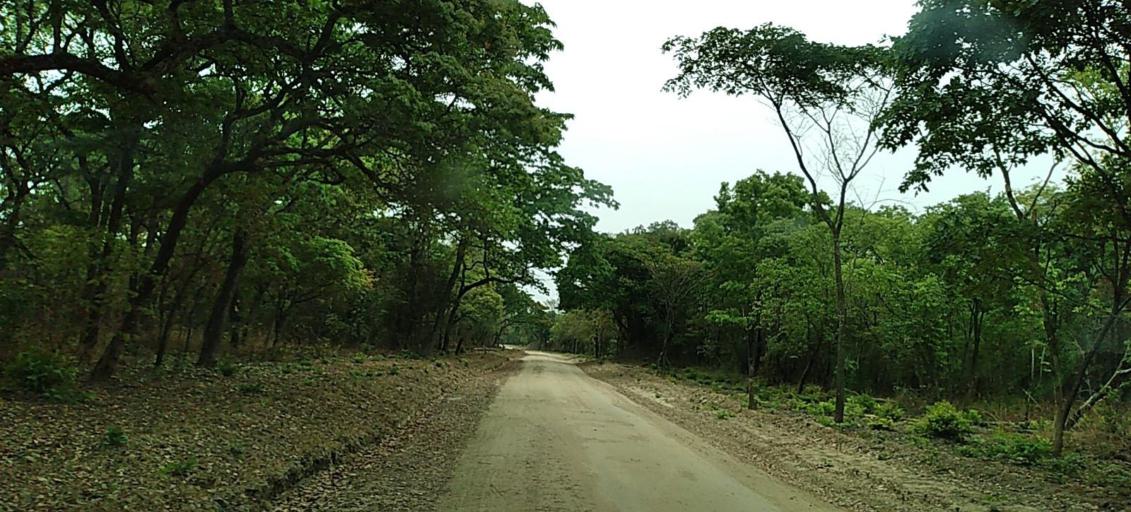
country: ZM
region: North-Western
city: Solwezi
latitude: -12.5338
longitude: 26.5231
